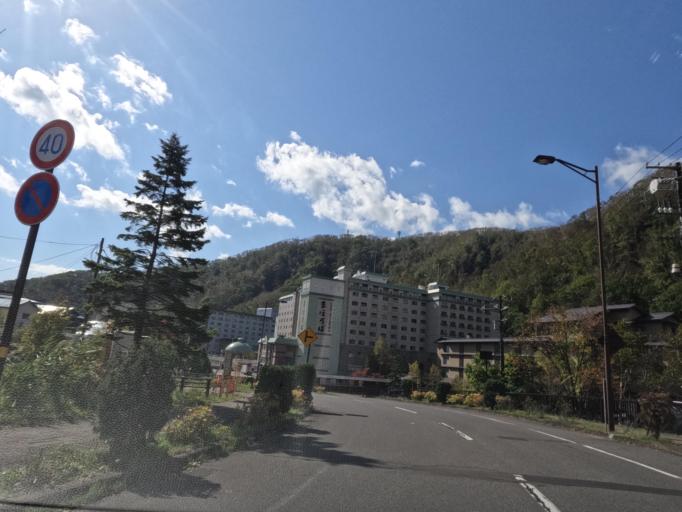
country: JP
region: Hokkaido
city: Shiraoi
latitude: 42.4948
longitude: 141.1428
